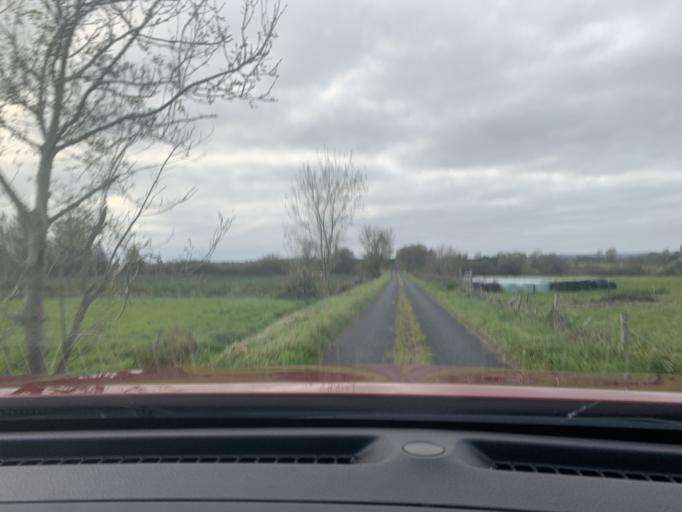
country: IE
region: Connaught
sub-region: Sligo
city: Tobercurry
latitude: 54.0158
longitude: -8.6195
